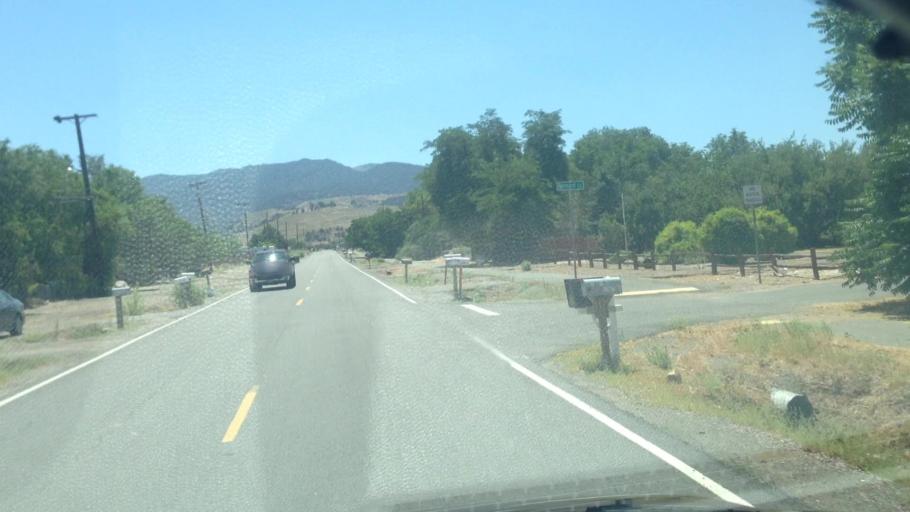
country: US
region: Nevada
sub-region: Storey County
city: Virginia City
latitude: 39.3821
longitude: -119.7223
